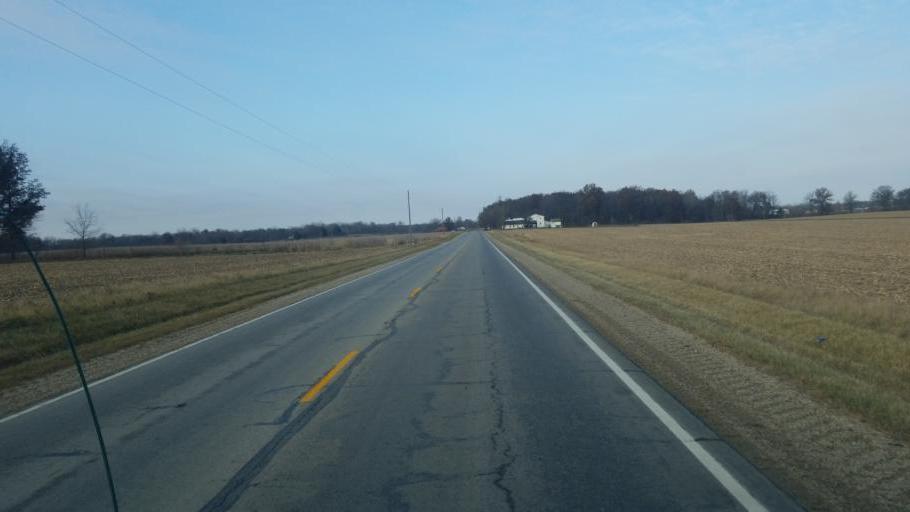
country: US
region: Indiana
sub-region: Adams County
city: Geneva
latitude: 40.5409
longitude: -84.9804
